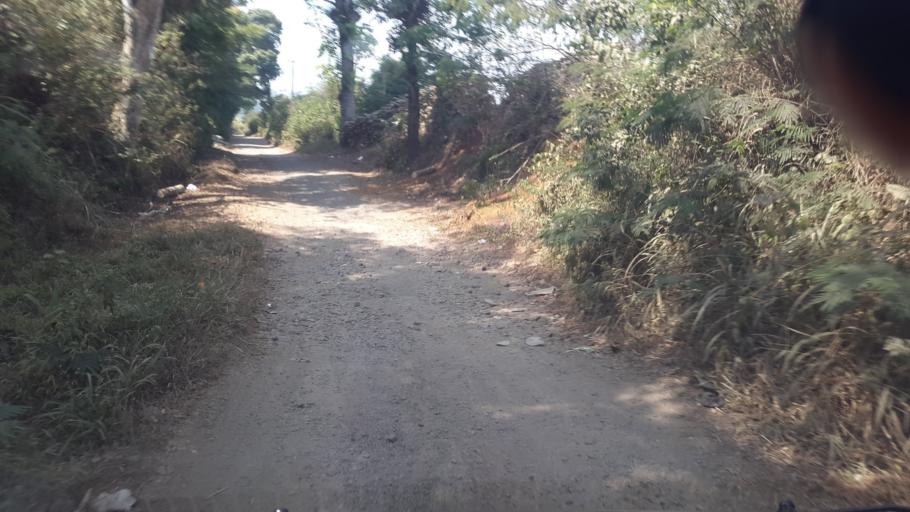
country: ID
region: West Java
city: Mekarjaya
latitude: -7.0122
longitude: 107.0242
